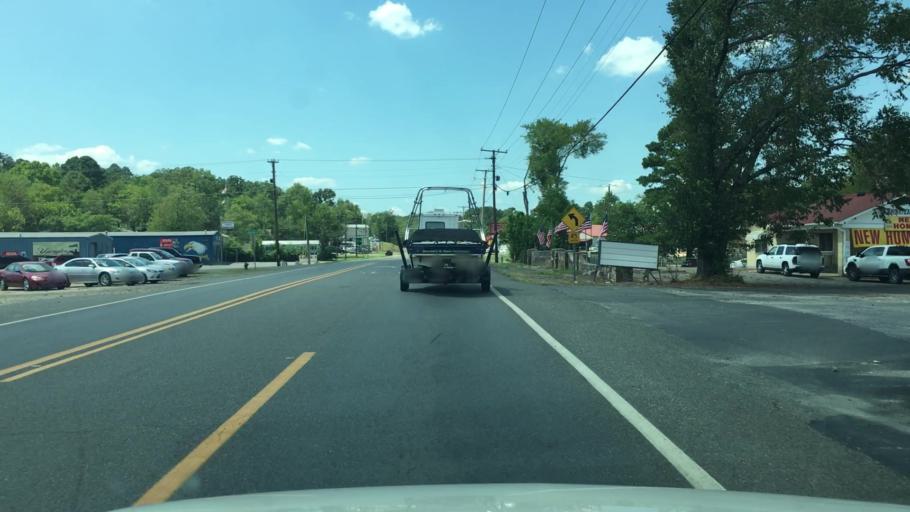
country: US
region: Arkansas
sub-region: Garland County
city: Piney
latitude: 34.5052
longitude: -93.1281
